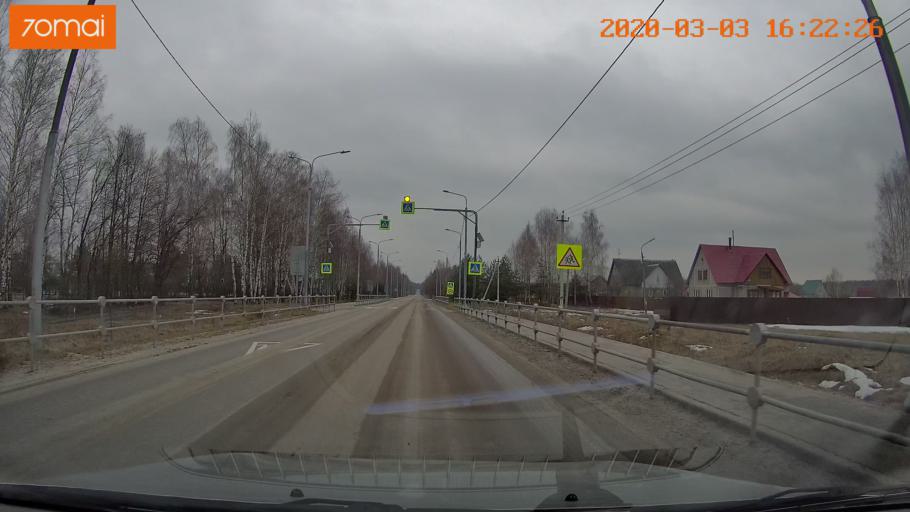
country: RU
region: Moskovskaya
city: Imeni Tsyurupy
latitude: 55.4916
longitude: 38.6481
